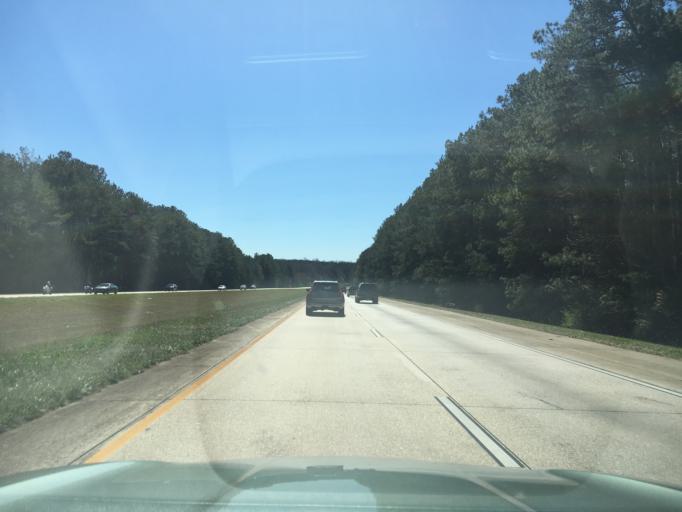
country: US
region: Georgia
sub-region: Troup County
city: Hogansville
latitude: 33.1043
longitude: -84.9067
